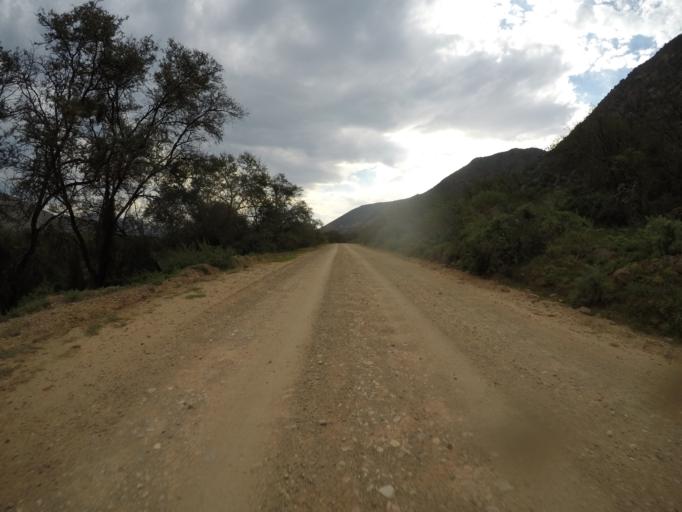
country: ZA
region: Eastern Cape
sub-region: Cacadu District Municipality
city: Kareedouw
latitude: -33.5752
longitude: 24.1395
